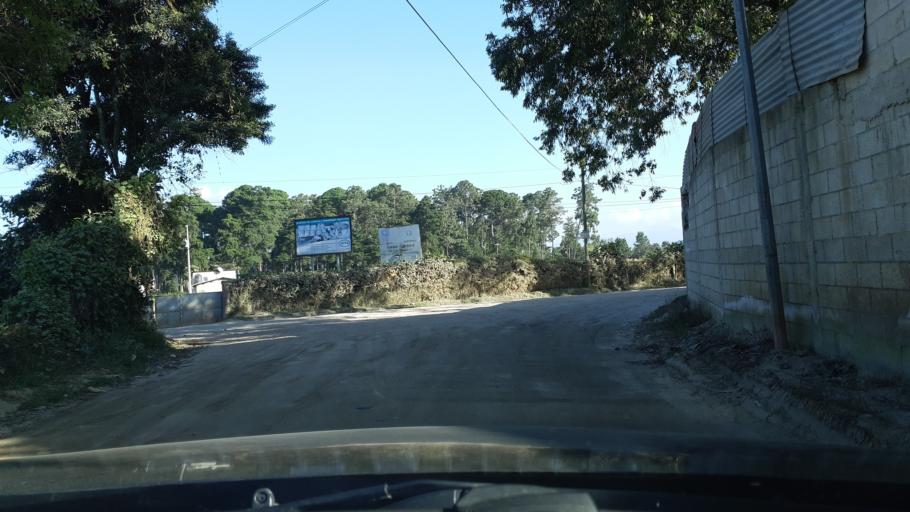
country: GT
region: Chimaltenango
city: El Tejar
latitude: 14.6366
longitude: -90.8002
